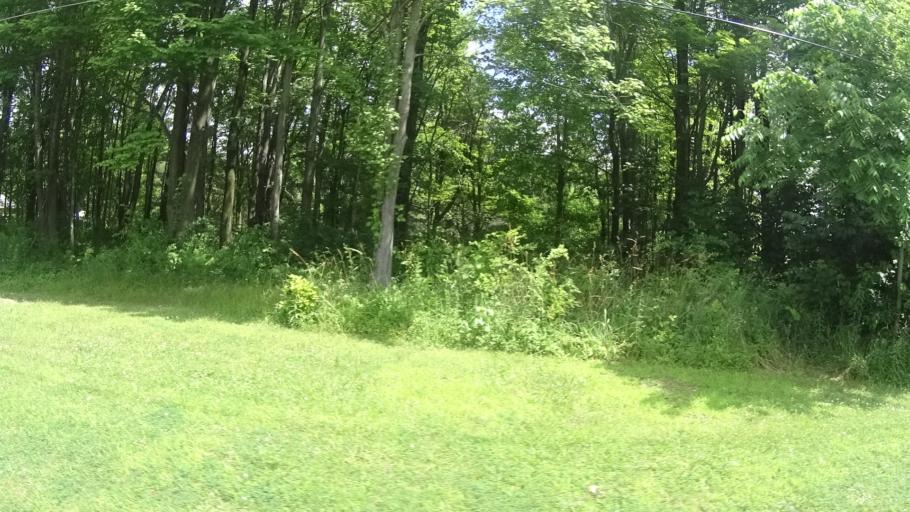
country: US
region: Ohio
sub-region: Huron County
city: Wakeman
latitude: 41.2938
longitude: -82.3784
